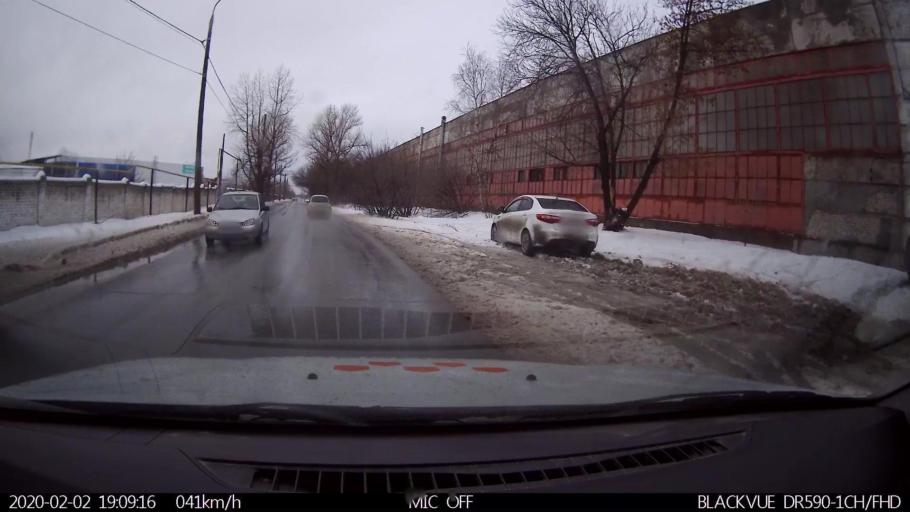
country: RU
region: Nizjnij Novgorod
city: Gorbatovka
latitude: 56.3462
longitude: 43.8220
